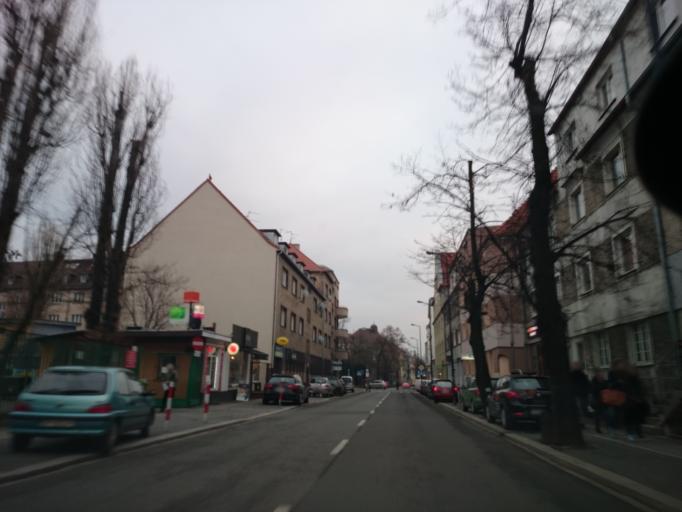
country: PL
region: Opole Voivodeship
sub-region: Powiat opolski
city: Opole
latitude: 50.6669
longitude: 17.9266
